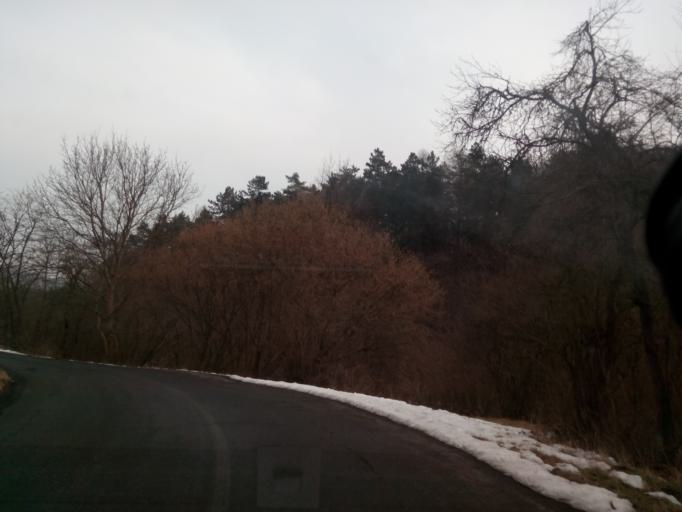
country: HU
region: Borsod-Abauj-Zemplen
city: Gonc
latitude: 48.4846
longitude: 21.3690
